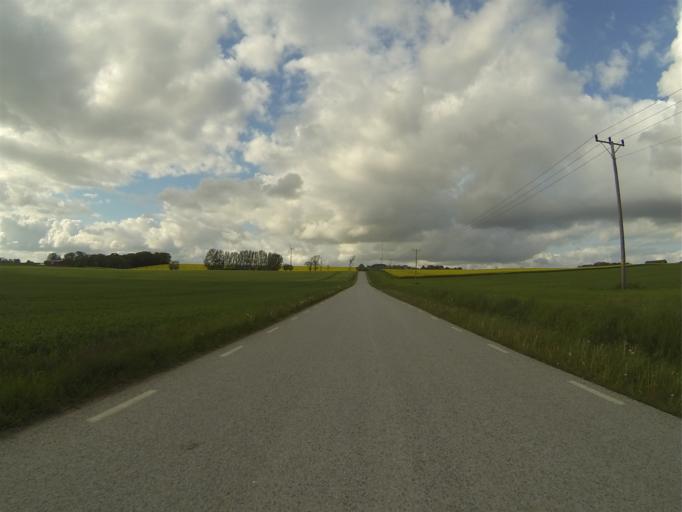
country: SE
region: Skane
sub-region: Staffanstorps Kommun
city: Staffanstorp
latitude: 55.6881
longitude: 13.2871
